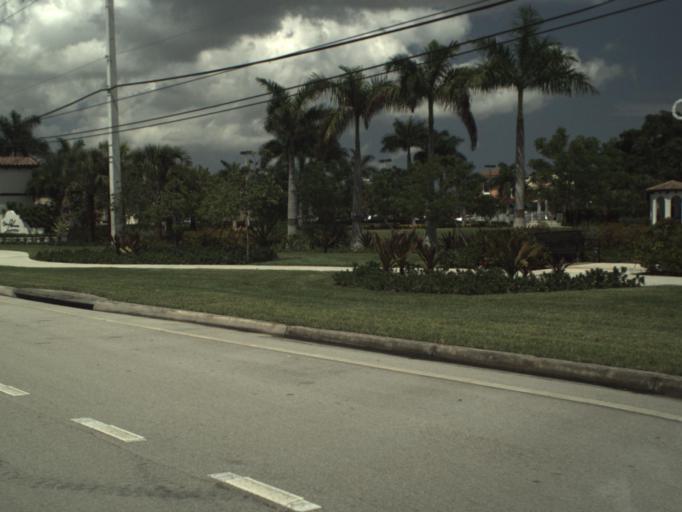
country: US
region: Florida
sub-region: Broward County
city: Parkland
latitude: 26.3055
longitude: -80.2021
